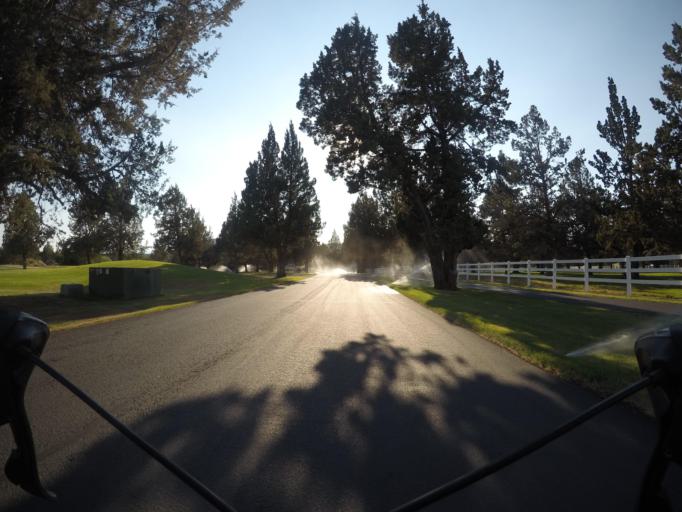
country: US
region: Oregon
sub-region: Deschutes County
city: Redmond
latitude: 44.2636
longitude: -121.2566
